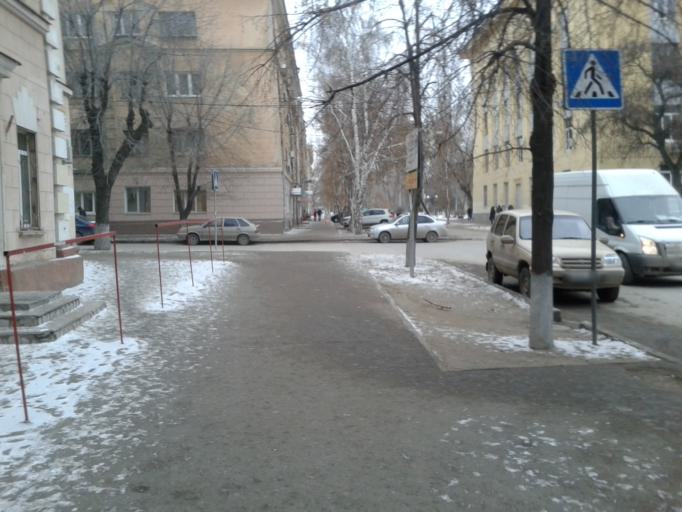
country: RU
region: Volgograd
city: Volgograd
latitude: 48.7064
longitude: 44.5116
